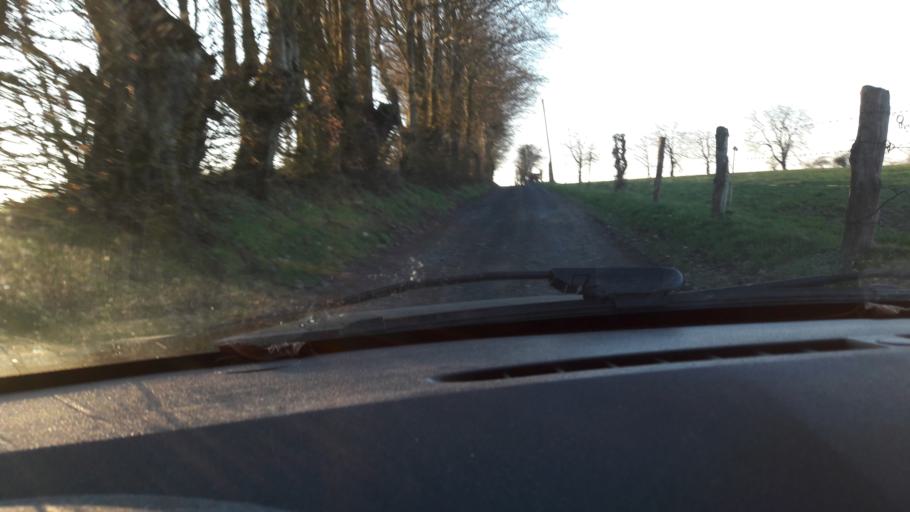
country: BE
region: Wallonia
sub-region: Province du Hainaut
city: Beaumont
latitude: 50.2452
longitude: 4.1900
